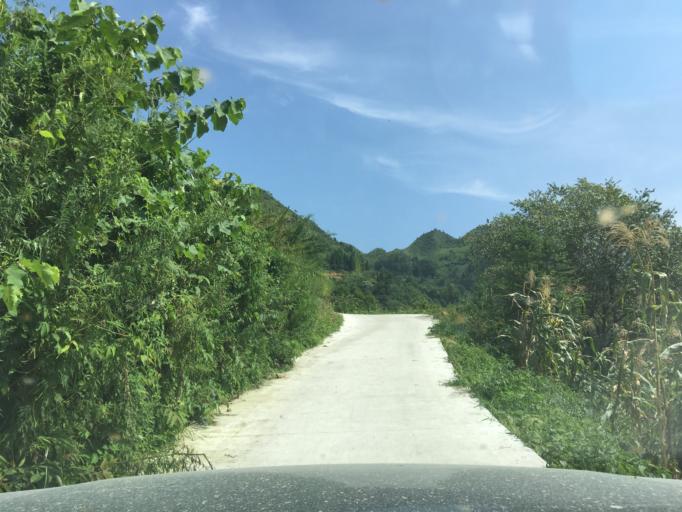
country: CN
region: Guangxi Zhuangzu Zizhiqu
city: Xinzhou
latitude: 24.9658
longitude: 105.6207
